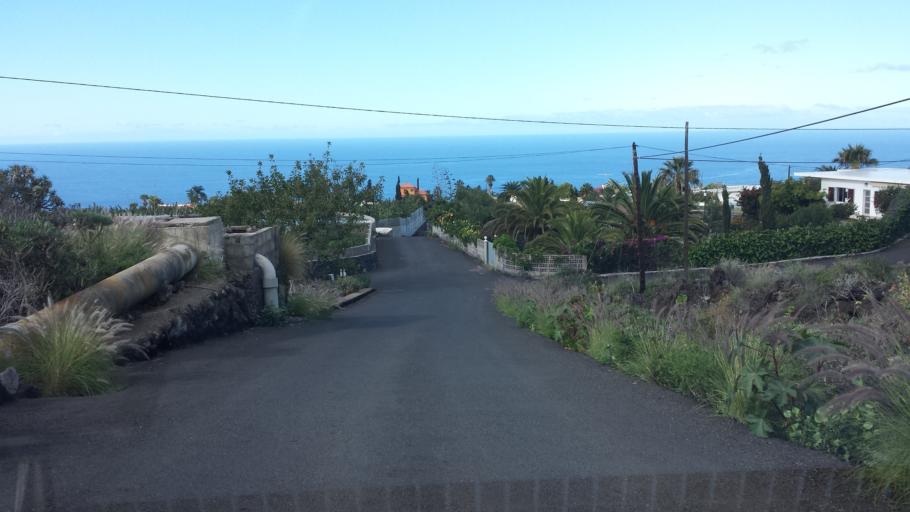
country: ES
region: Canary Islands
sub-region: Provincia de Santa Cruz de Tenerife
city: Tazacorte
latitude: 28.6078
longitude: -17.9049
